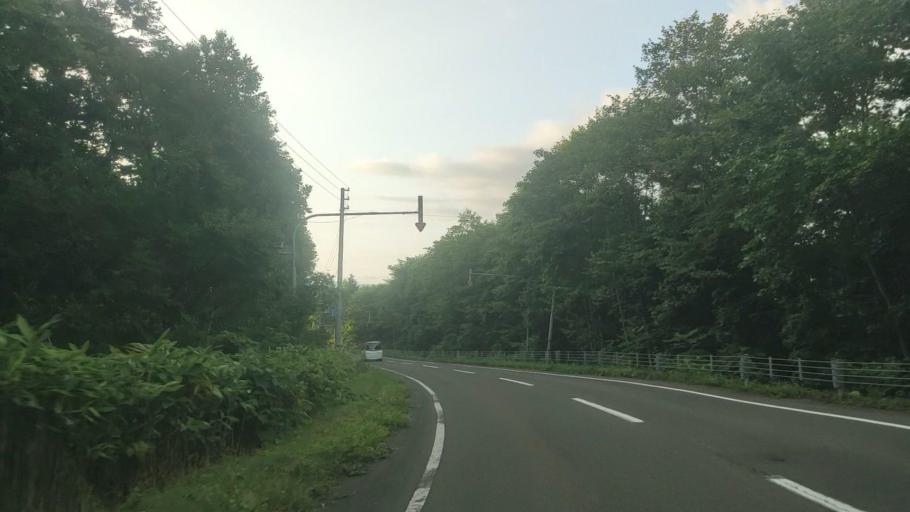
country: JP
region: Hokkaido
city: Bibai
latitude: 43.1765
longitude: 142.0701
